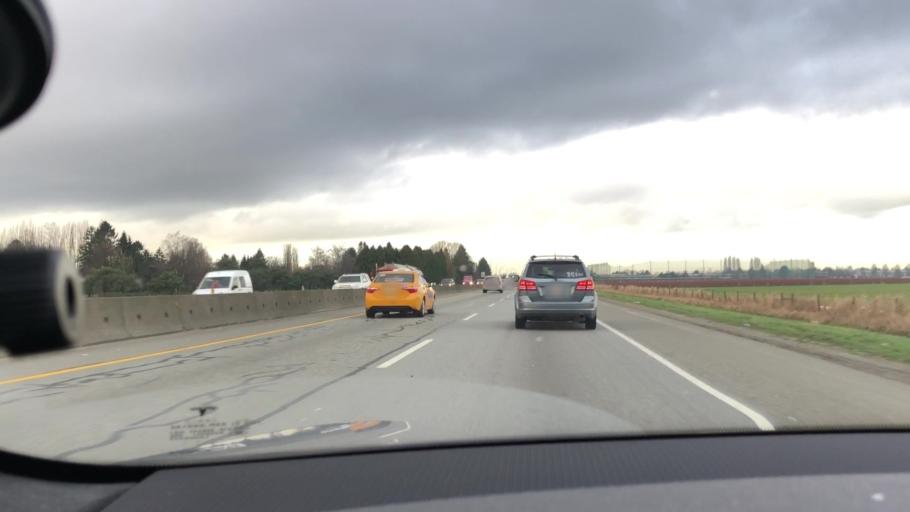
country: CA
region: British Columbia
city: Richmond
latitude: 49.1779
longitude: -123.0551
